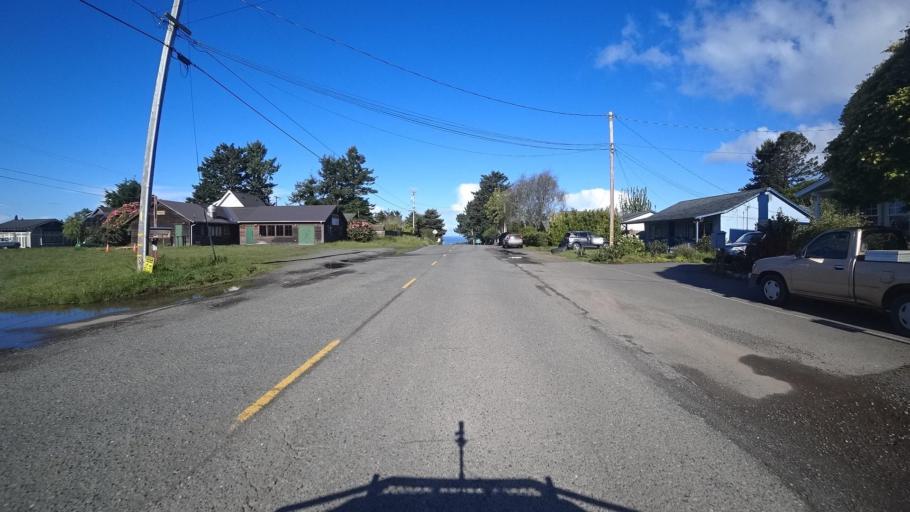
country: US
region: California
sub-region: Humboldt County
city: Westhaven-Moonstone
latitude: 41.0358
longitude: -124.1101
